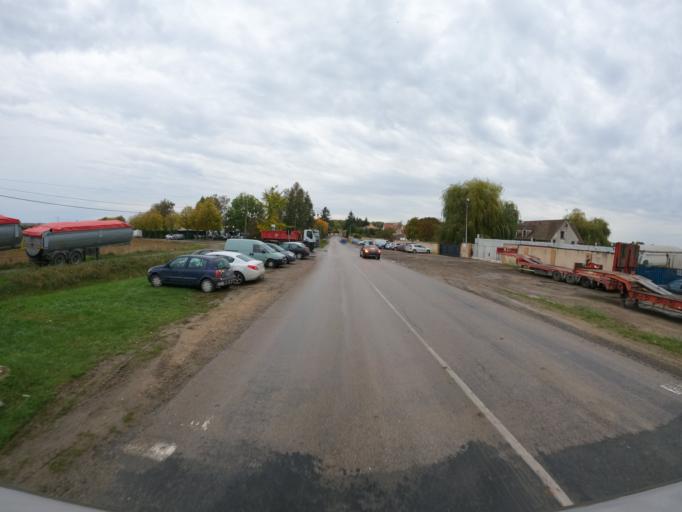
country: FR
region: Ile-de-France
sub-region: Departement de Seine-et-Marne
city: Chanteloup-en-Brie
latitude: 48.8322
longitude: 2.7548
